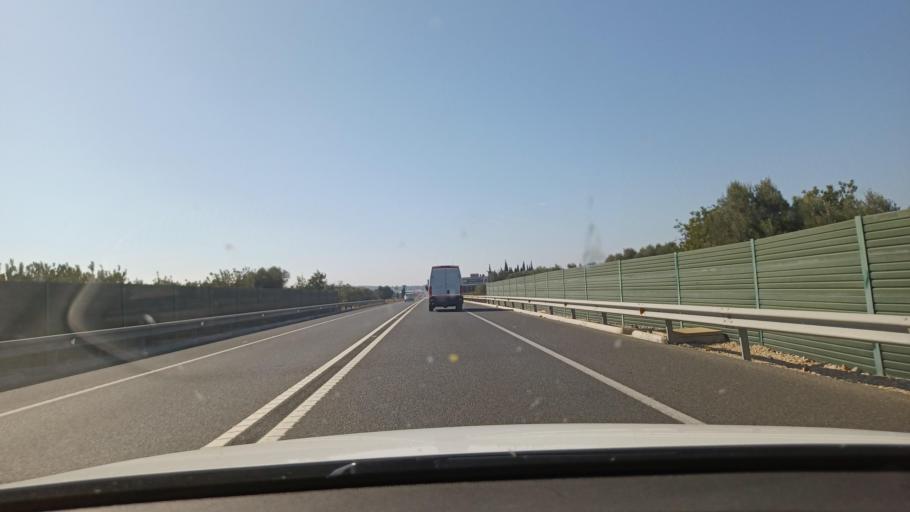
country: ES
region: Catalonia
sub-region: Provincia de Tarragona
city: Camarles
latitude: 40.7566
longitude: 0.6189
